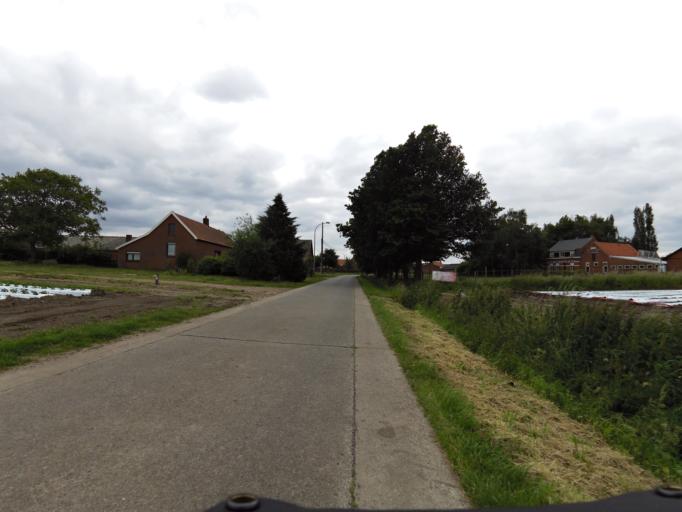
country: BE
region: Flanders
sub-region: Provincie Antwerpen
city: Baarle-Hertog
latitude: 51.4786
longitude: 4.8300
